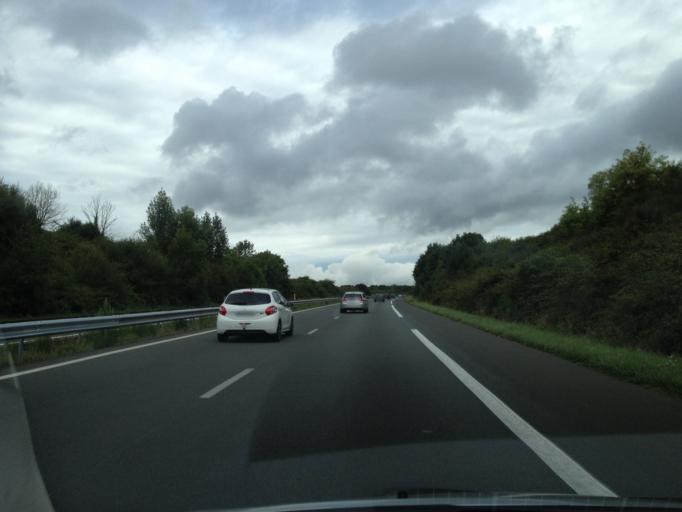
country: FR
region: Aquitaine
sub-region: Departement du Lot-et-Garonne
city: Fourques-sur-Garonne
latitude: 44.3801
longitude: 0.2132
